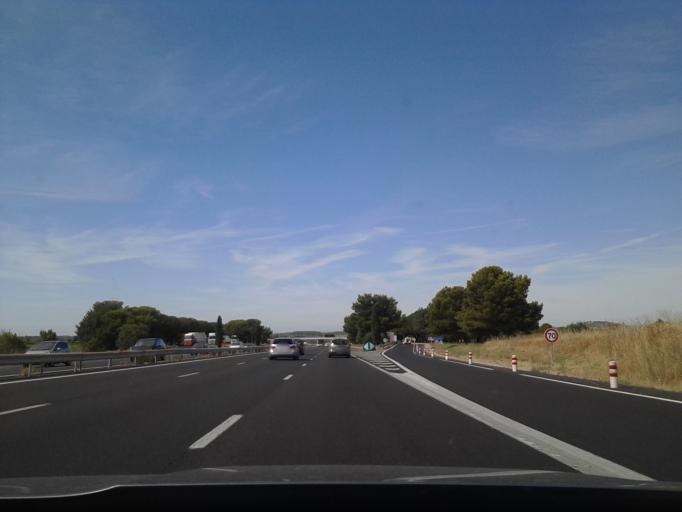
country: FR
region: Languedoc-Roussillon
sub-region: Departement de l'Herault
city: Florensac
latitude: 43.3983
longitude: 3.4717
